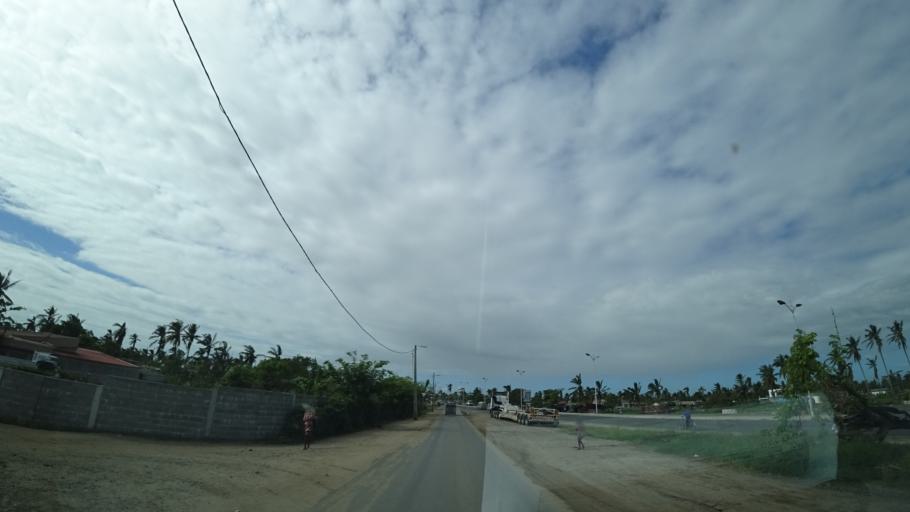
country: MZ
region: Sofala
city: Beira
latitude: -19.7818
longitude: 34.8787
